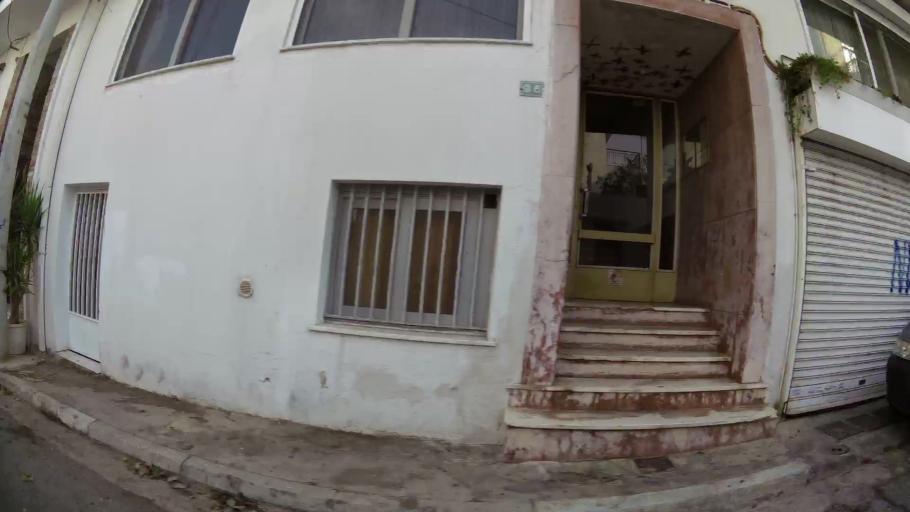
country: GR
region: Attica
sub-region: Nomarchia Athinas
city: Galatsi
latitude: 37.9968
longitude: 23.7582
